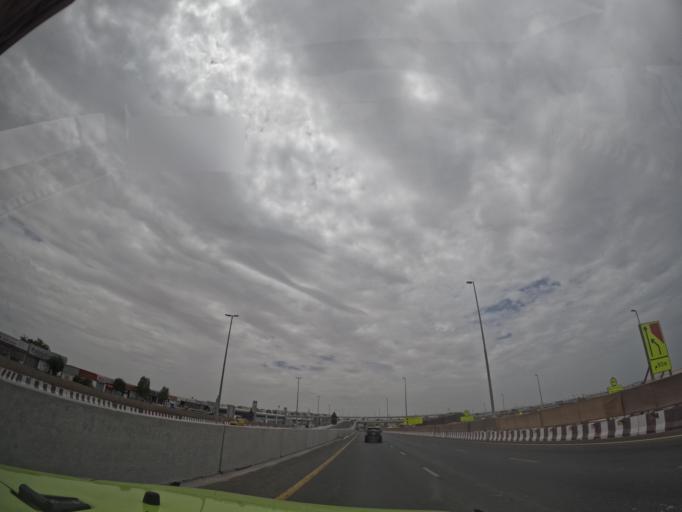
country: AE
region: Ash Shariqah
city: Sharjah
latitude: 25.1936
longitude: 55.3715
